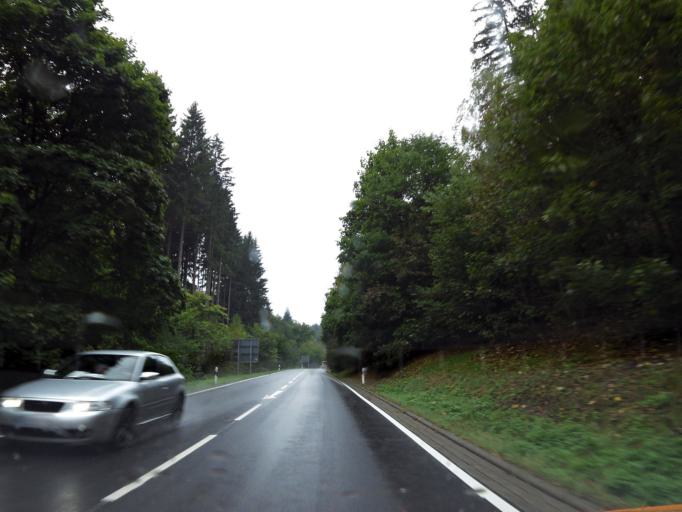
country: DE
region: Saxony-Anhalt
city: Harzgerode
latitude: 51.6450
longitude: 11.1067
